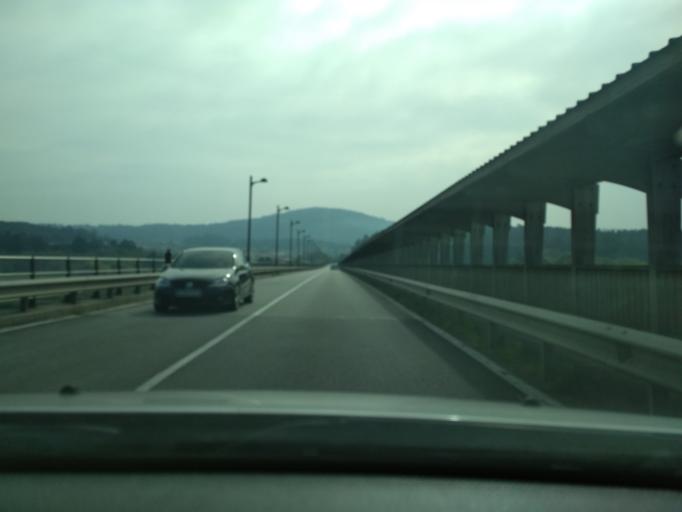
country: ES
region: Galicia
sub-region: Provincia de Pontevedra
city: Catoira
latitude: 42.6771
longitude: -8.7259
